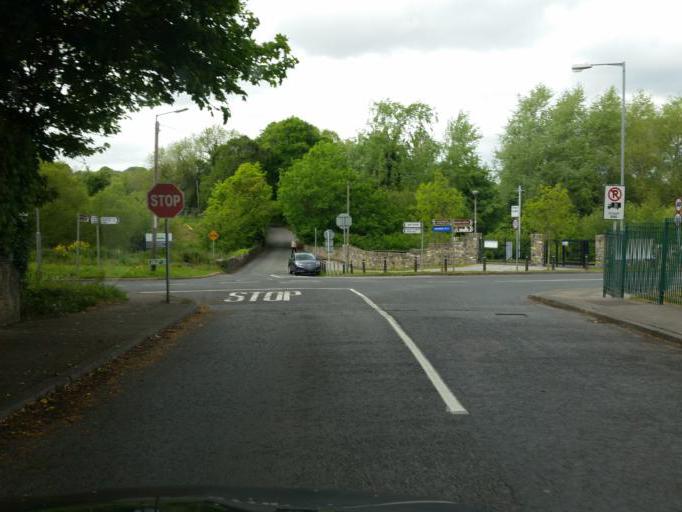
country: IE
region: Leinster
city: Castleknock
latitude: 53.3771
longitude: -6.3333
